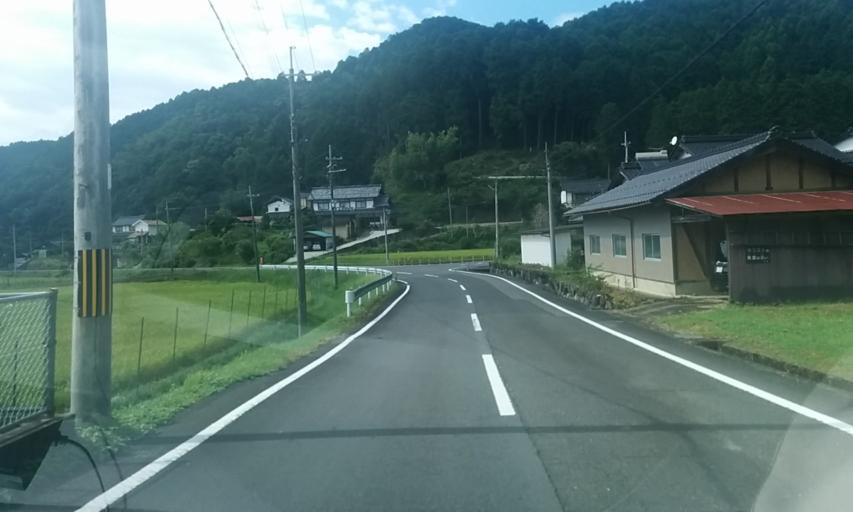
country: JP
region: Kyoto
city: Fukuchiyama
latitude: 35.3730
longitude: 135.1573
